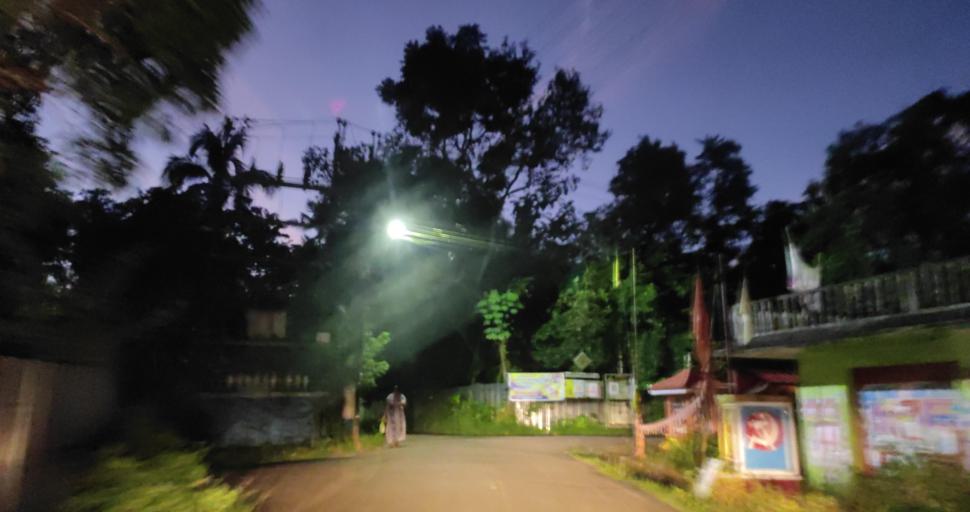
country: IN
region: Kerala
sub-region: Alappuzha
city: Shertallai
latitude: 9.6229
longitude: 76.3520
